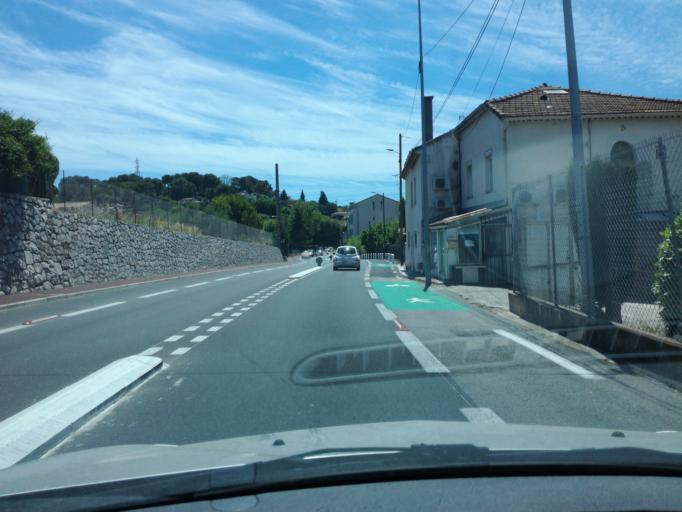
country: FR
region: Provence-Alpes-Cote d'Azur
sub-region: Departement des Alpes-Maritimes
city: Mougins
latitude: 43.5916
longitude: 7.0025
